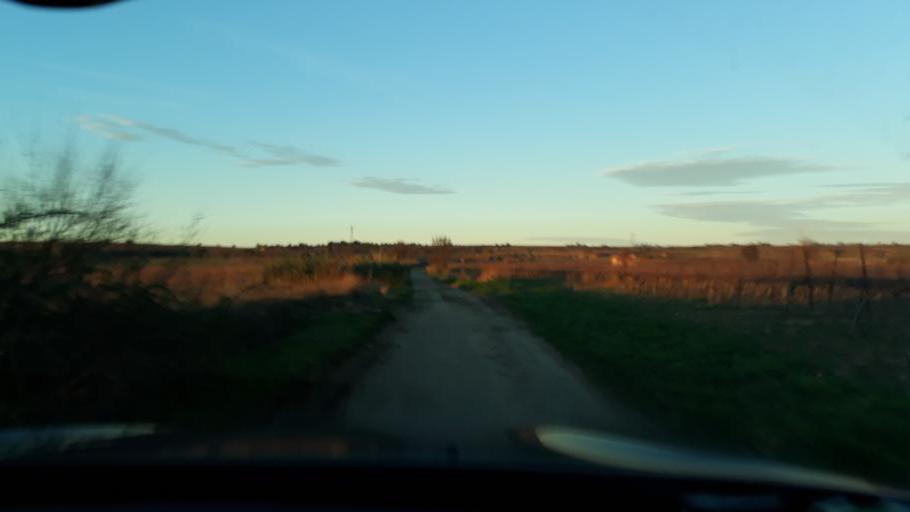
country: FR
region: Languedoc-Roussillon
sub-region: Departement de l'Herault
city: Florensac
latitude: 43.4028
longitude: 3.4597
